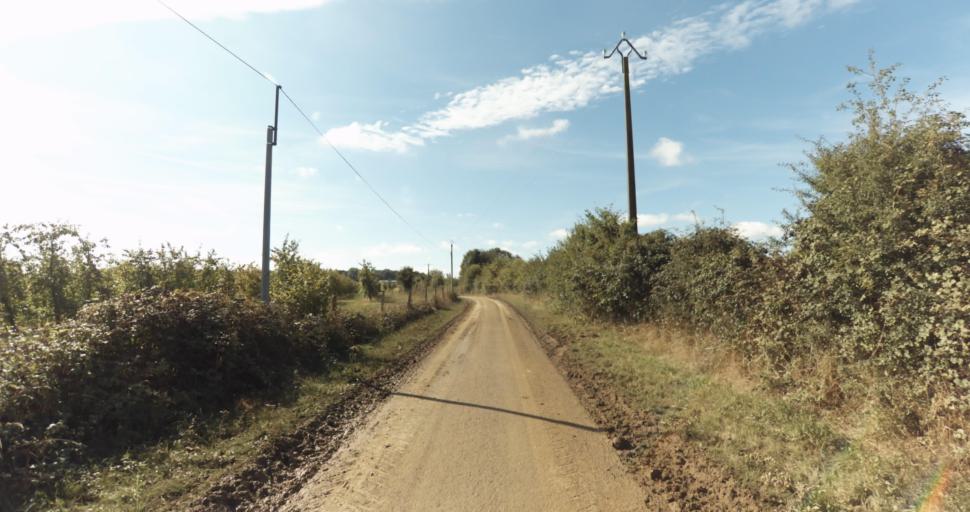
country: FR
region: Lower Normandy
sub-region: Departement du Calvados
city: Orbec
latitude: 48.9308
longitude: 0.3597
